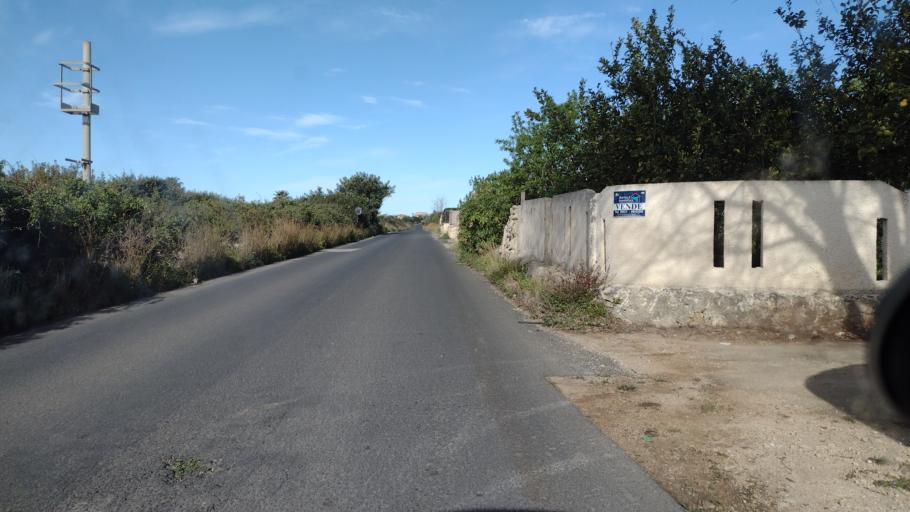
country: IT
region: Sicily
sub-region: Provincia di Siracusa
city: Avola
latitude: 36.8725
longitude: 15.1218
